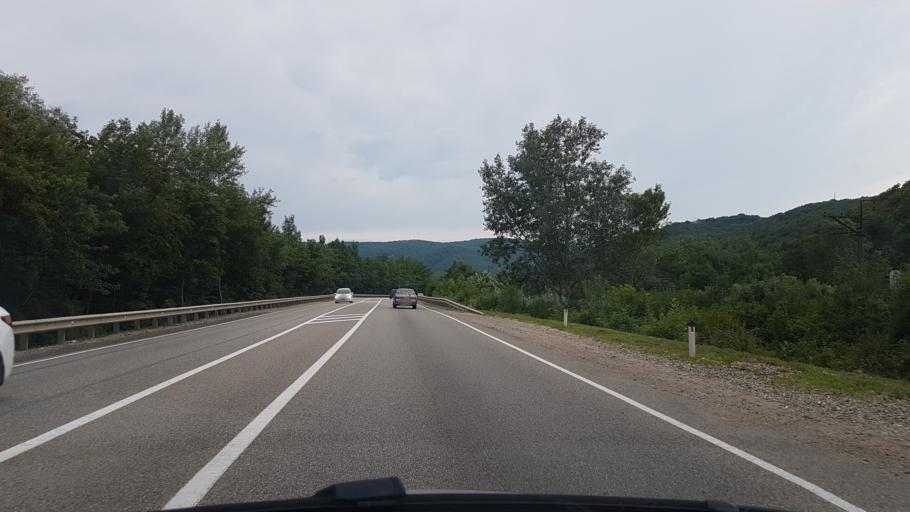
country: RU
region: Krasnodarskiy
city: Goryachiy Klyuch
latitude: 44.6175
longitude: 39.0867
